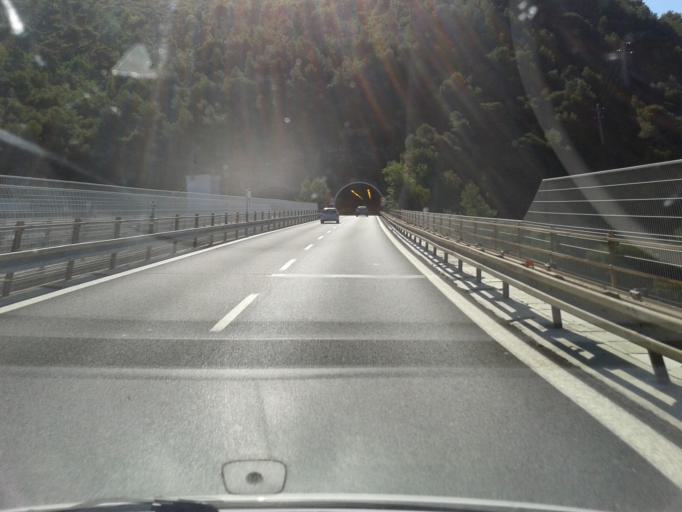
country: IT
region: Liguria
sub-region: Provincia di Imperia
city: Camporosso
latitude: 43.8010
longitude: 7.6332
